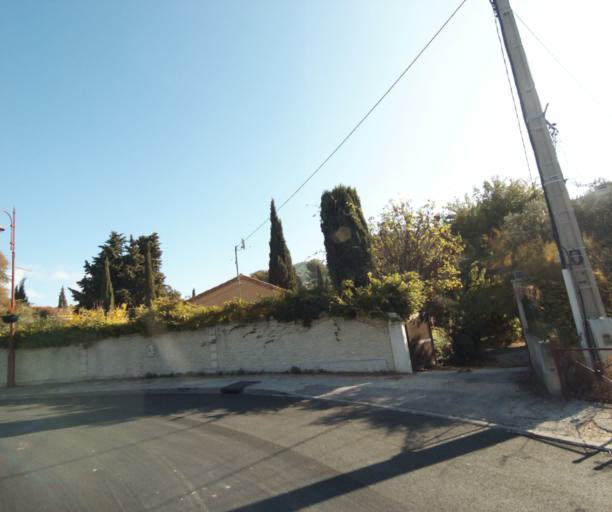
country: FR
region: Provence-Alpes-Cote d'Azur
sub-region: Departement des Bouches-du-Rhone
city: Allauch
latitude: 43.3384
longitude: 5.4800
